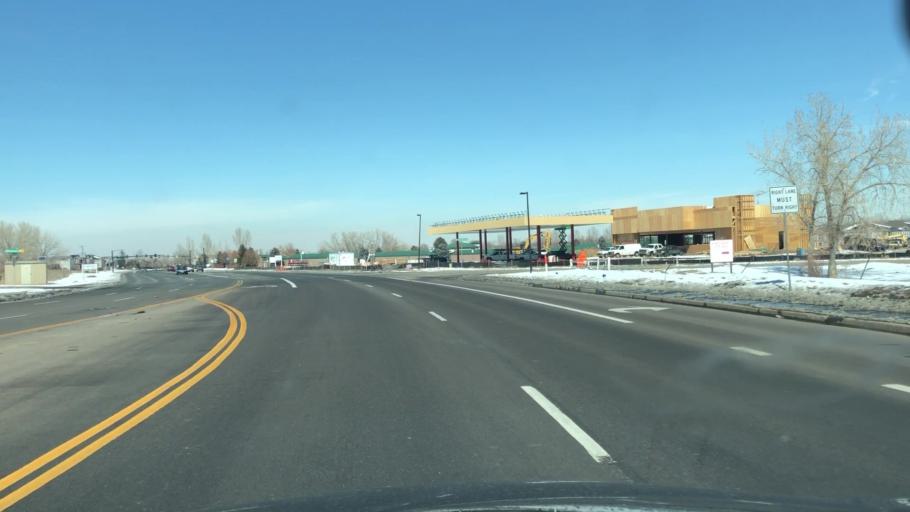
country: US
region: Colorado
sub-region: Douglas County
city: Stonegate
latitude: 39.5509
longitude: -104.7934
